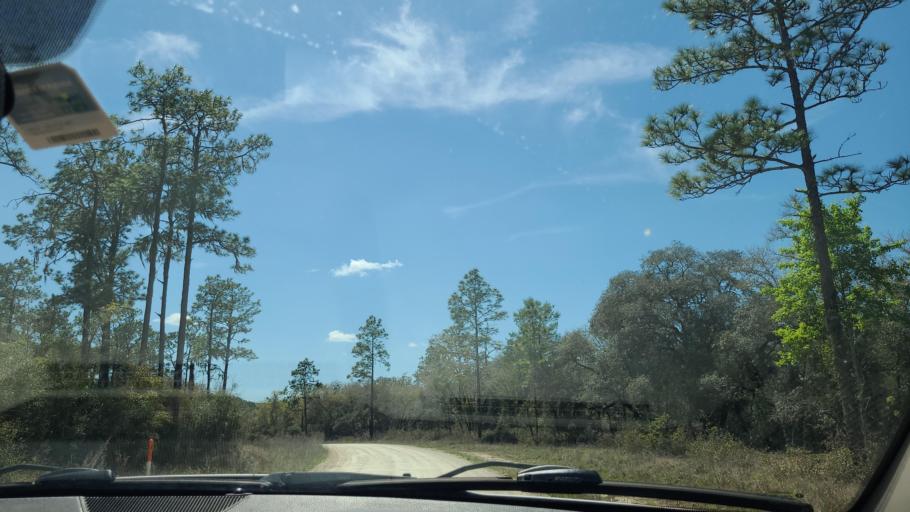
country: US
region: Florida
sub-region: Putnam County
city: Interlachen
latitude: 29.4327
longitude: -81.7854
